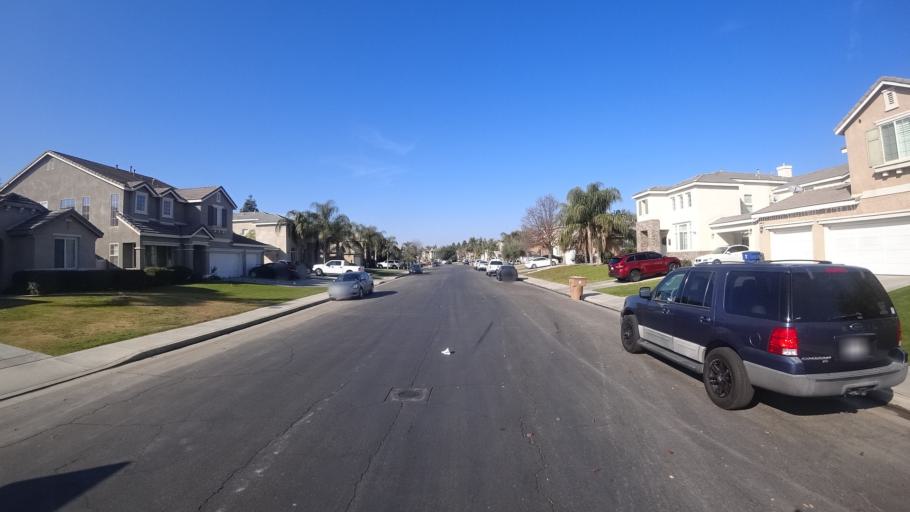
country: US
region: California
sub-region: Kern County
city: Greenacres
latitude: 35.3164
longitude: -119.1209
